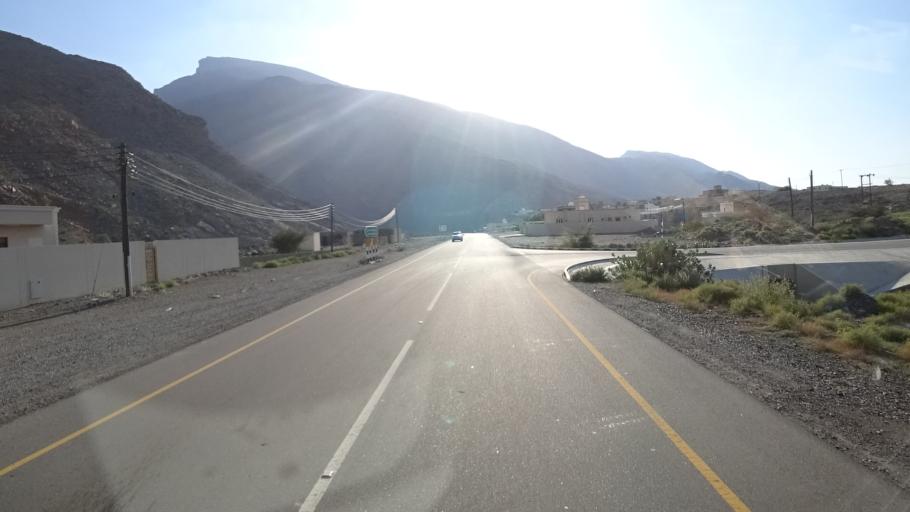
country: OM
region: Al Batinah
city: Rustaq
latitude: 23.3855
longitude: 57.3073
